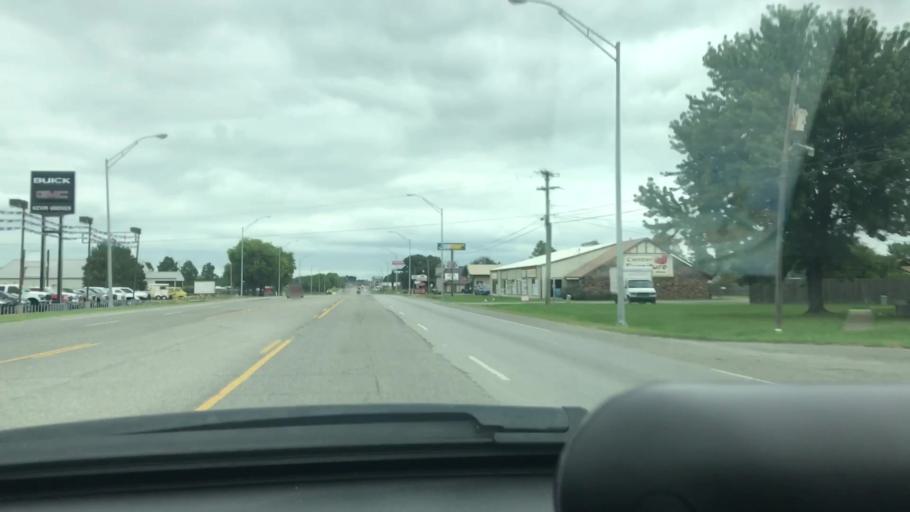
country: US
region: Oklahoma
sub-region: Wagoner County
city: Wagoner
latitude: 35.9455
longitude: -95.3952
